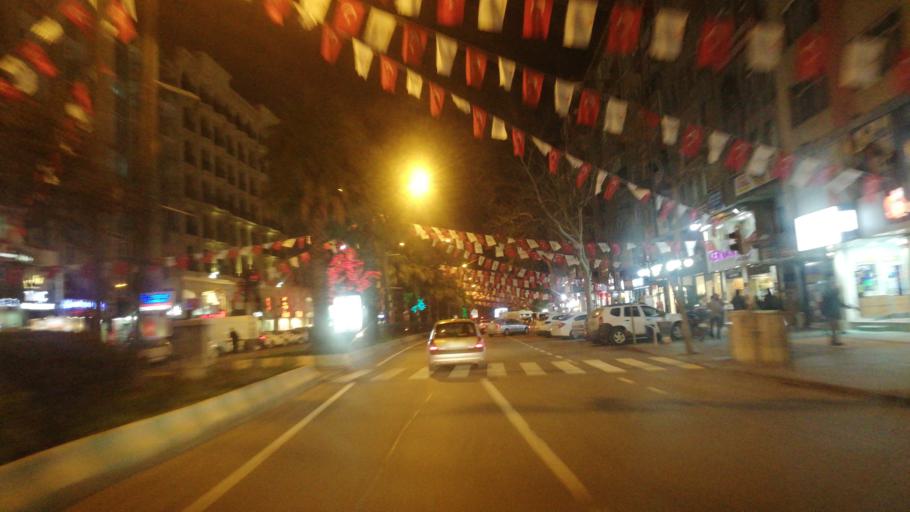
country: TR
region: Kahramanmaras
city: Kahramanmaras
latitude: 37.5769
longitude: 36.9316
